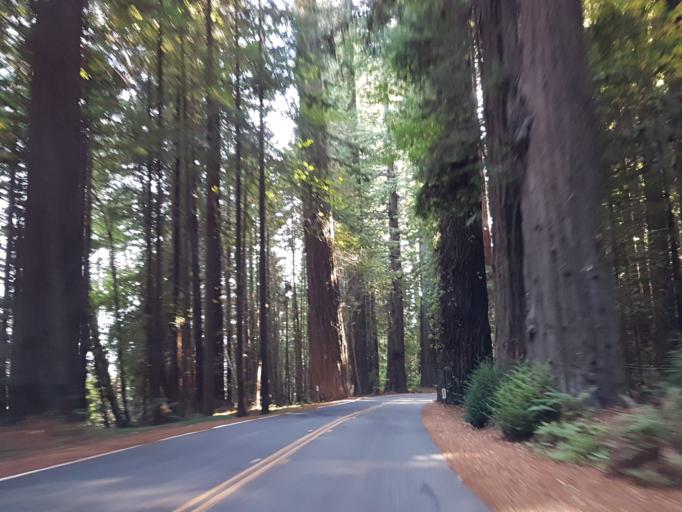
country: US
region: California
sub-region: Humboldt County
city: Rio Dell
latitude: 40.4417
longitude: -123.9856
